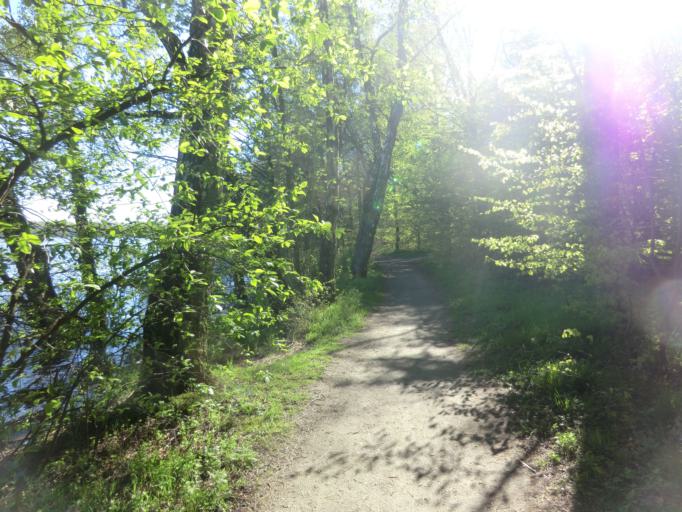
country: SE
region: Skane
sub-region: Sjobo Kommun
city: Sjoebo
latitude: 55.5672
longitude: 13.7188
